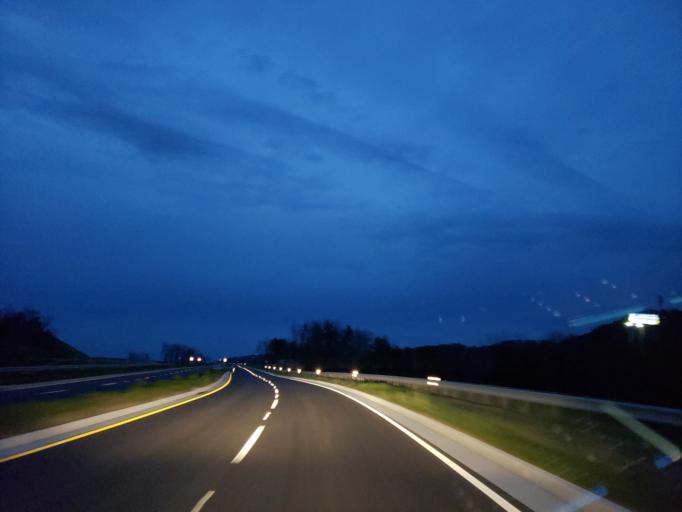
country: US
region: Georgia
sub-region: Bartow County
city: Emerson
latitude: 34.1268
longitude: -84.7413
